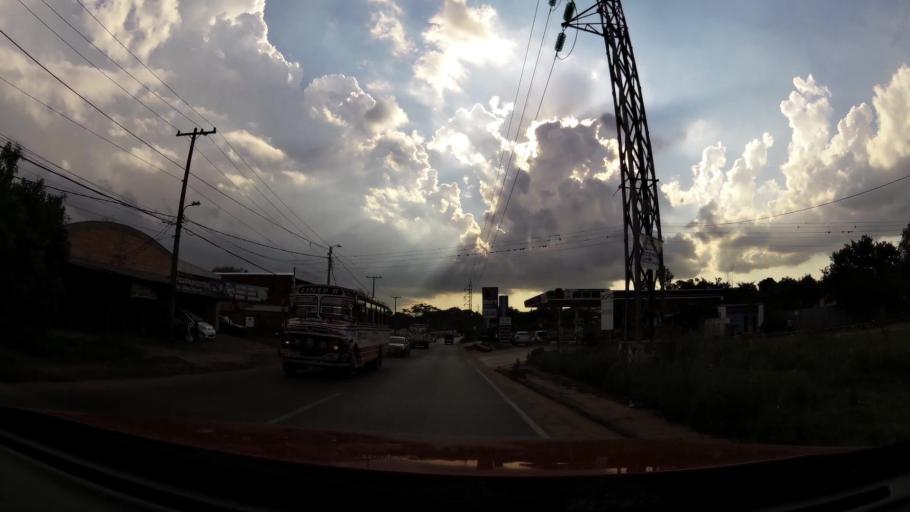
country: PY
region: Central
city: Villa Elisa
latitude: -25.3564
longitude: -57.5587
